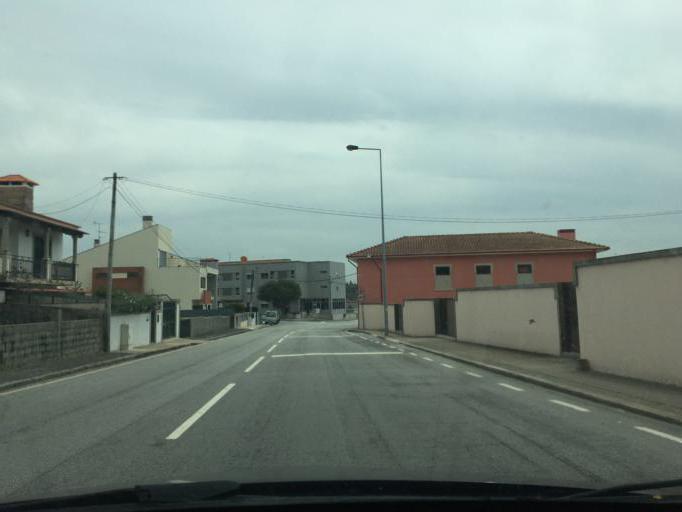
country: PT
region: Porto
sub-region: Maia
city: Anta
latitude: 41.2635
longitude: -8.6223
